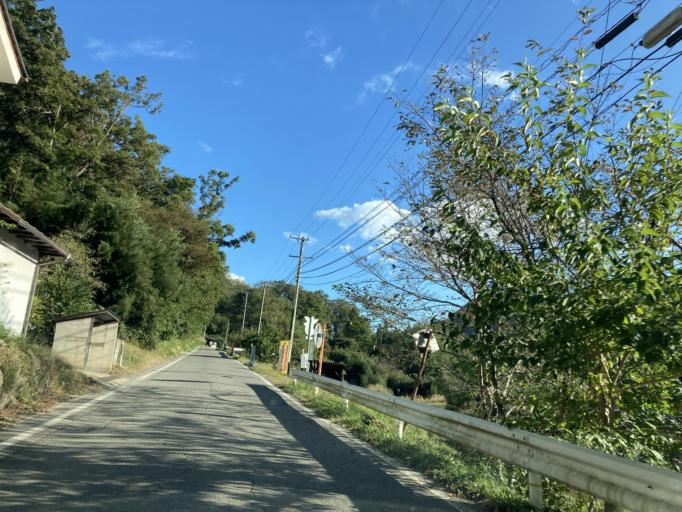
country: JP
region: Nagano
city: Omachi
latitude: 36.4444
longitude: 137.9828
